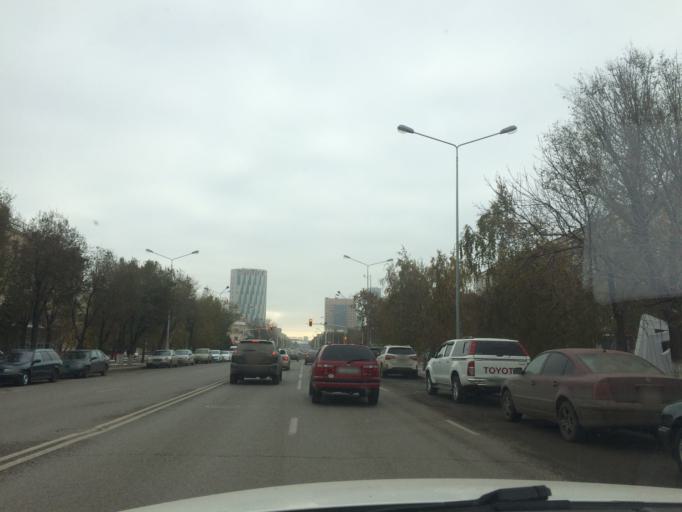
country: KZ
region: Astana Qalasy
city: Astana
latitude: 51.1748
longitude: 71.4189
